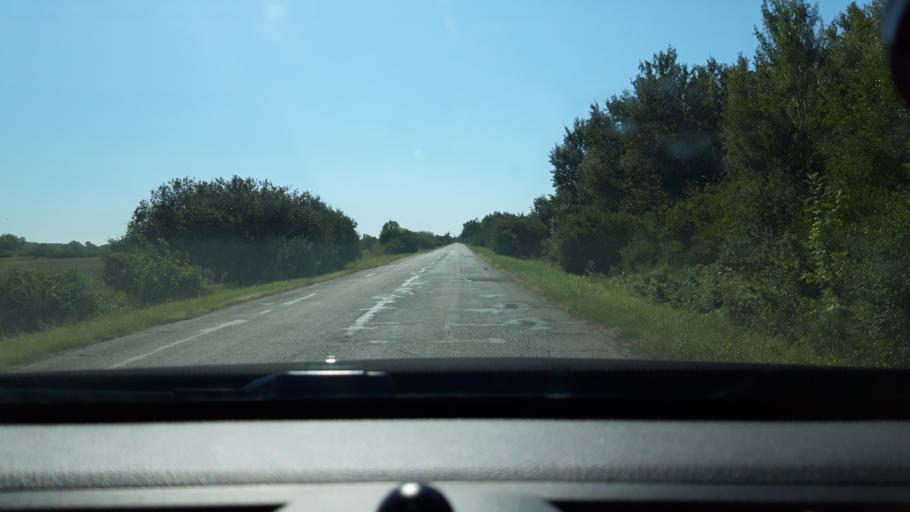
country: SK
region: Kosicky
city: Michalovce
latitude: 48.6248
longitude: 21.9360
